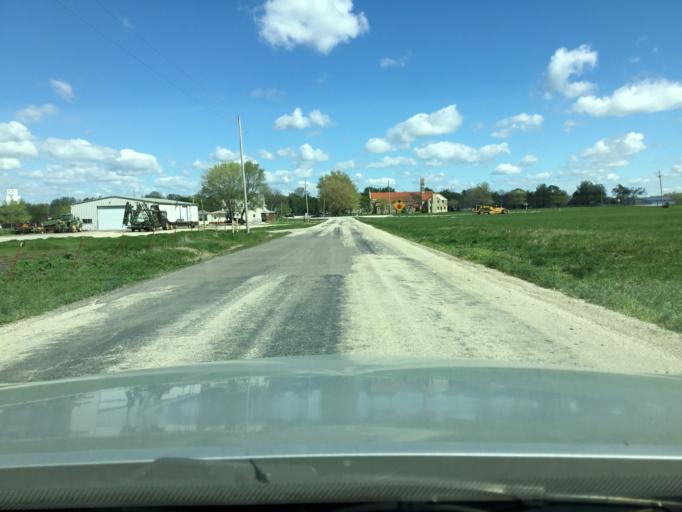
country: US
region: Kansas
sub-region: Anderson County
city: Garnett
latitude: 38.3589
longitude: -95.1253
